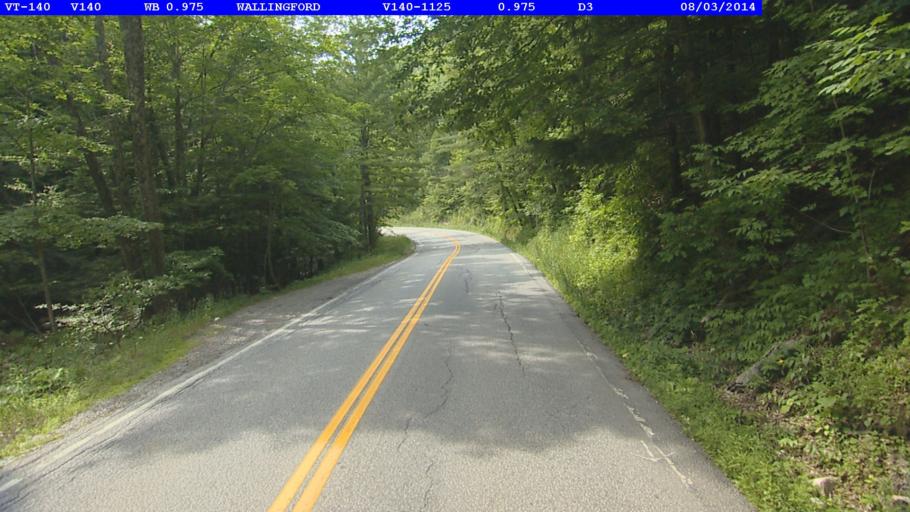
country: US
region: Vermont
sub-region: Rutland County
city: Rutland
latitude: 43.4668
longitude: -72.9599
